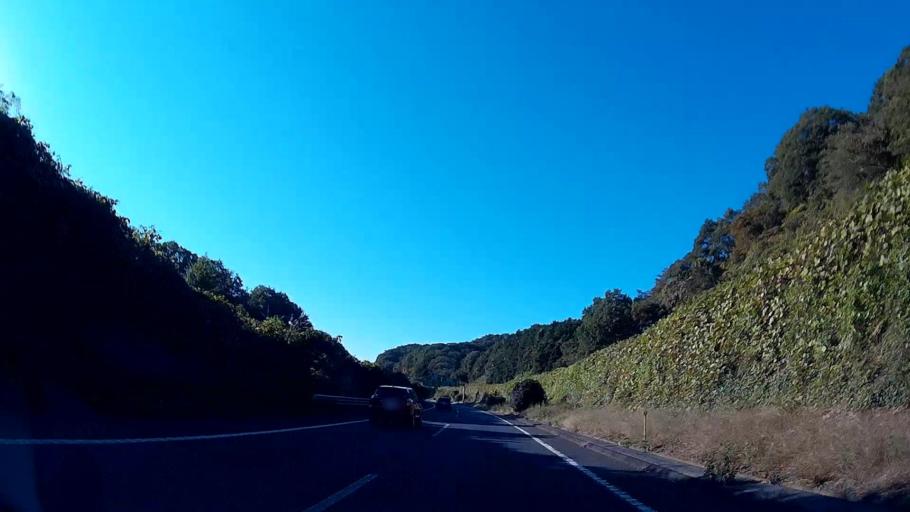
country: JP
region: Tokyo
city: Hachioji
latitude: 35.6509
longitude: 139.2662
